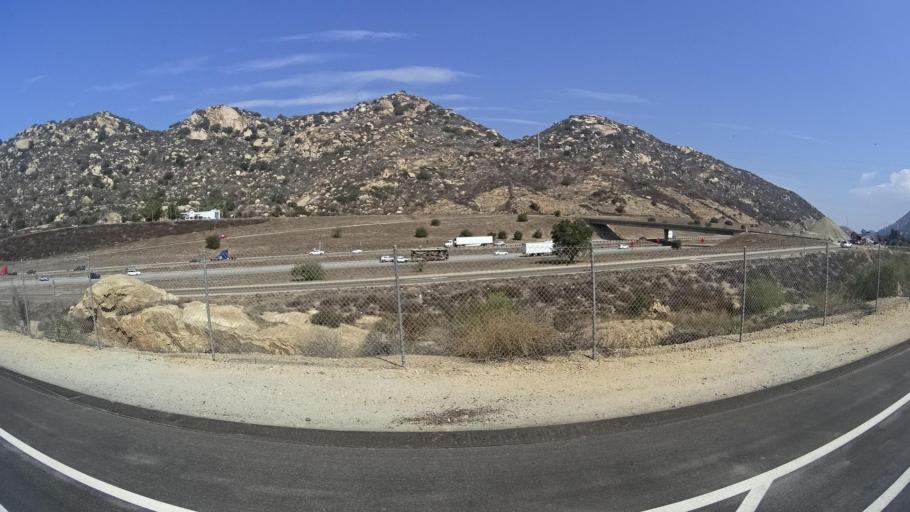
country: US
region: California
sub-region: San Diego County
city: Rainbow
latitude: 33.4286
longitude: -117.1455
